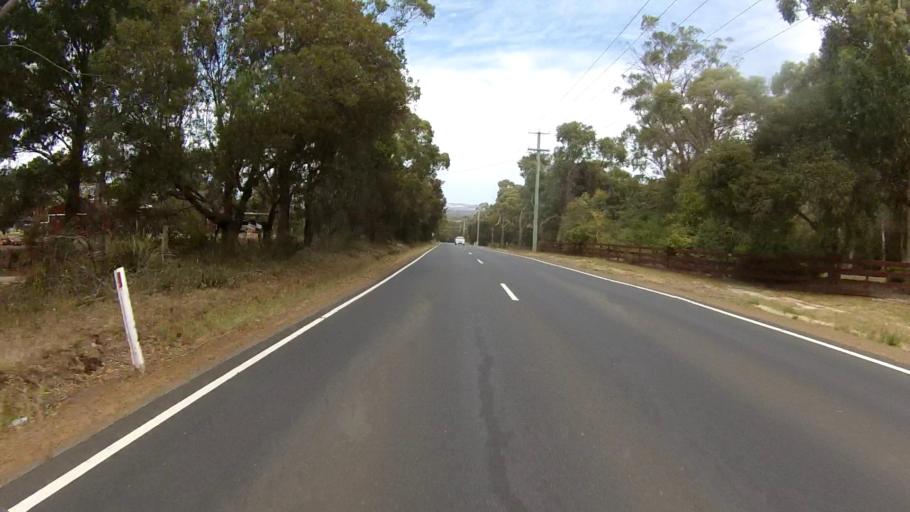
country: AU
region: Tasmania
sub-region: Clarence
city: Acton Park
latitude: -42.8812
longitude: 147.4821
